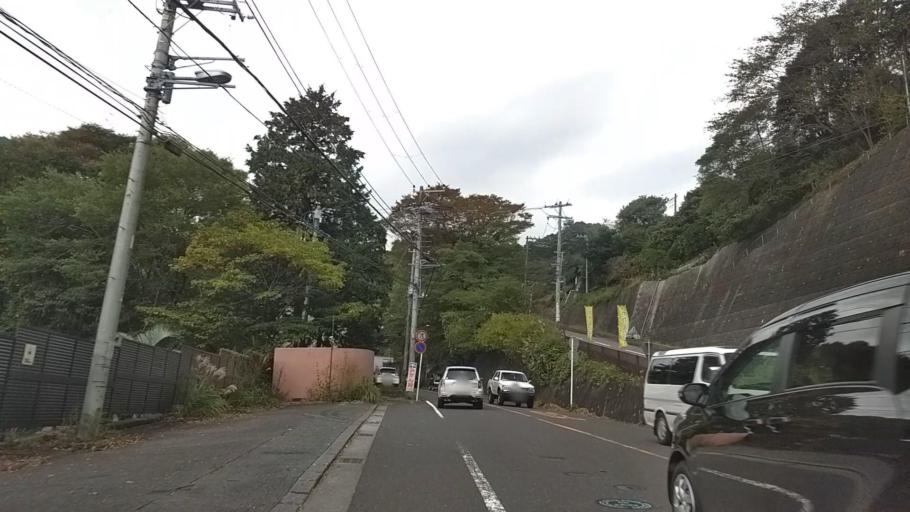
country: JP
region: Kanagawa
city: Odawara
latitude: 35.2013
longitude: 139.1327
